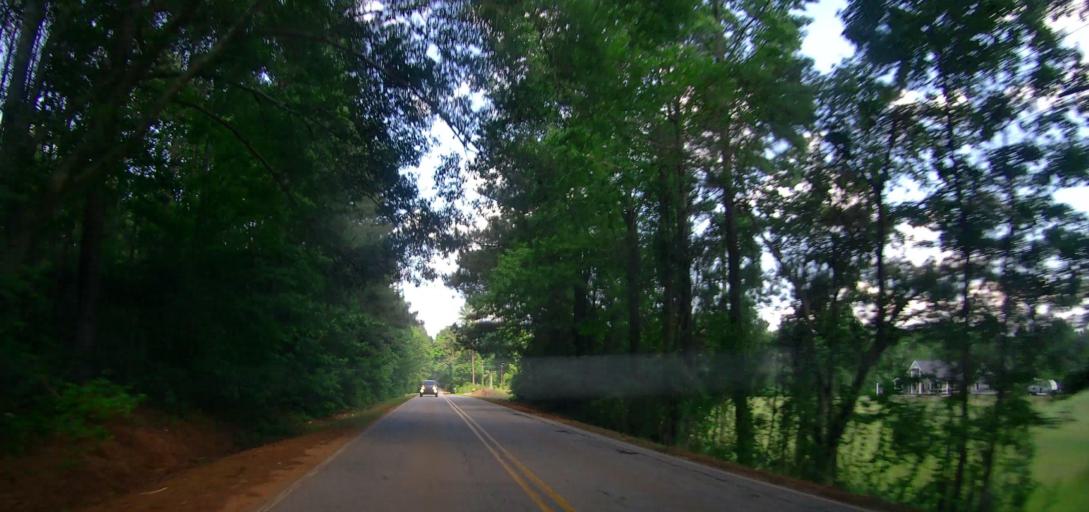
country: US
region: Georgia
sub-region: Spalding County
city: East Griffin
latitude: 33.2355
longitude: -84.1546
